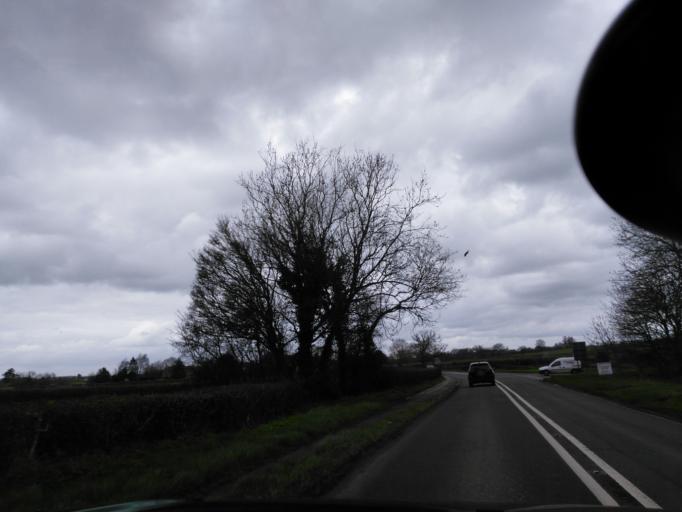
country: GB
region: England
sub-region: Wiltshire
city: Malmesbury
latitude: 51.5679
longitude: -2.0994
